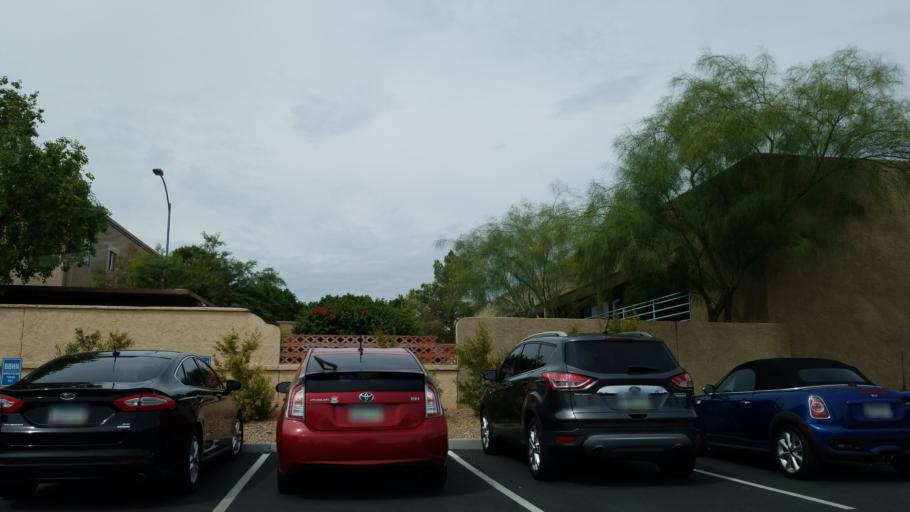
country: US
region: Arizona
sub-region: Maricopa County
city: Scottsdale
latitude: 33.4835
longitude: -111.9196
